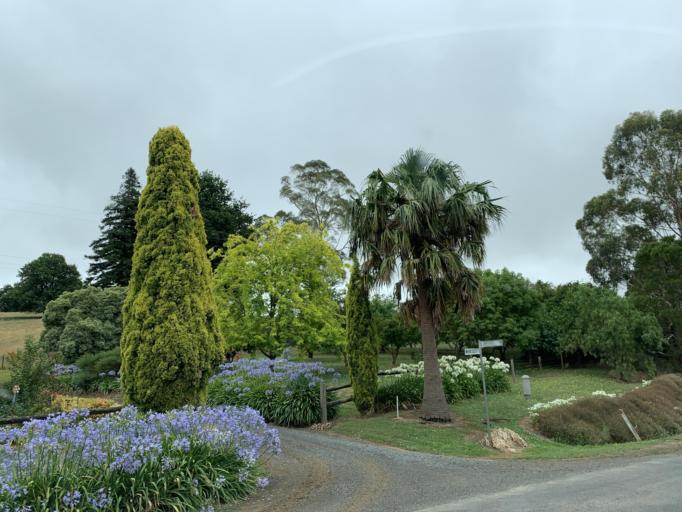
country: AU
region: Victoria
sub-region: Baw Baw
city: Warragul
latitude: -38.3209
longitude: 145.8311
